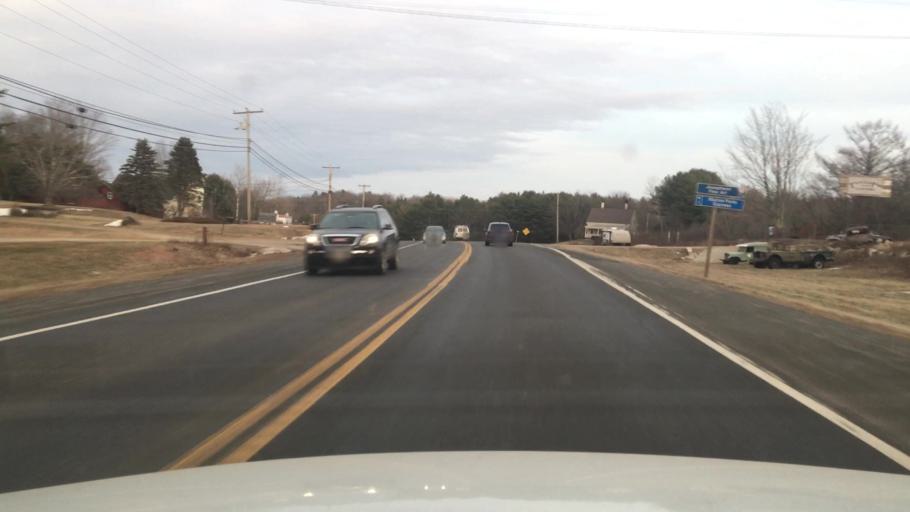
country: US
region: Maine
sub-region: Lincoln County
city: Edgecomb
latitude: 44.0024
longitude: -69.6139
